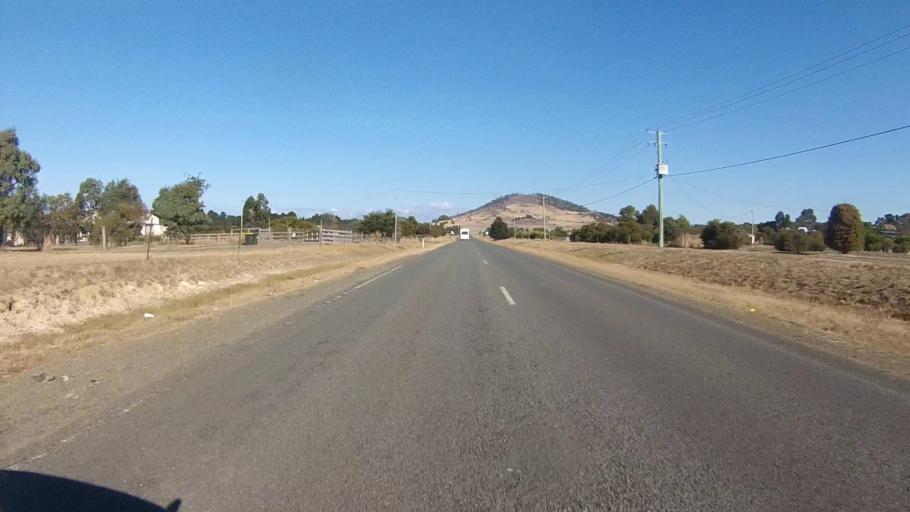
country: AU
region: Tasmania
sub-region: Clarence
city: Seven Mile Beach
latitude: -42.8517
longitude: 147.4855
